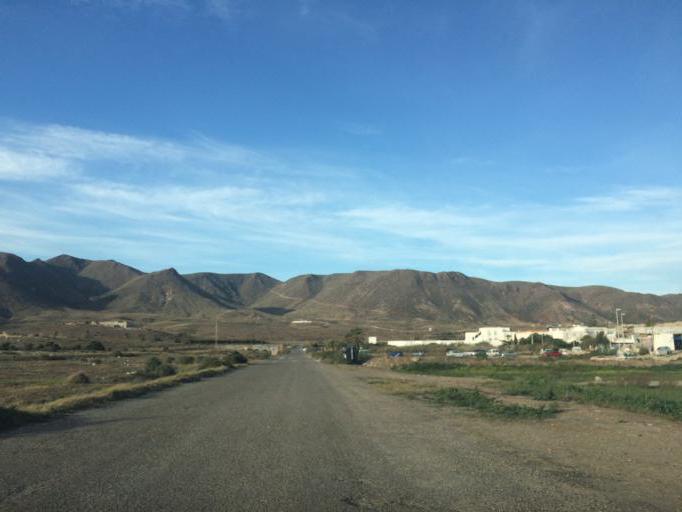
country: ES
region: Andalusia
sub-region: Provincia de Almeria
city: San Jose
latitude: 36.8013
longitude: -2.0639
